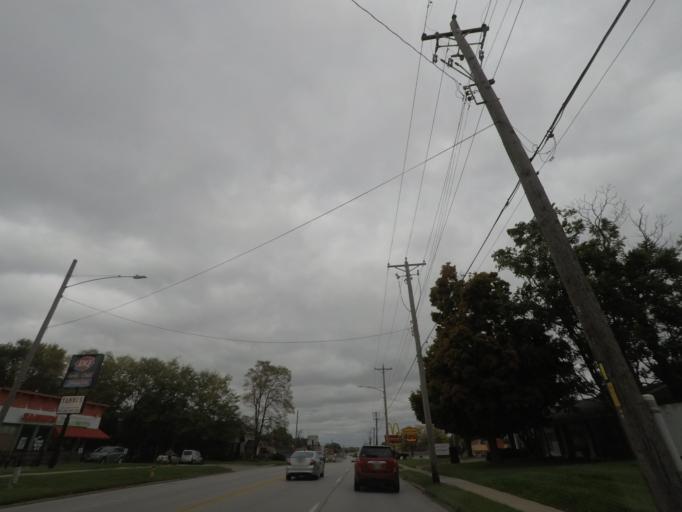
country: US
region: Iowa
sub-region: Polk County
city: Ankeny
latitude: 41.7273
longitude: -93.6003
